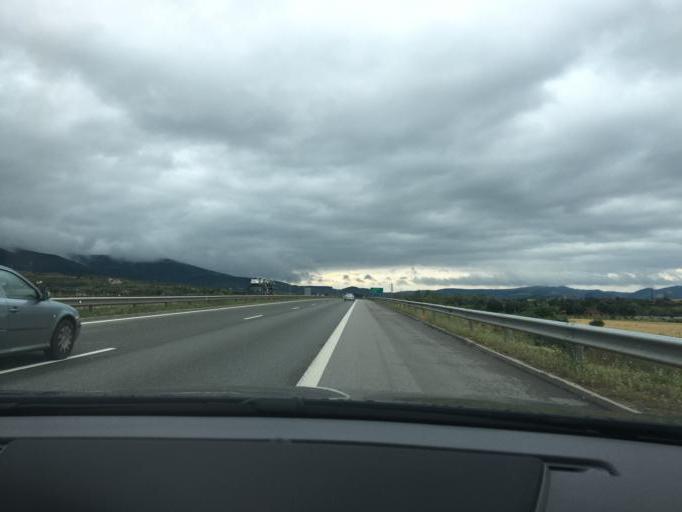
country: BG
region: Sofiya
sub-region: Obshtina Bozhurishte
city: Bozhurishte
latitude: 42.6925
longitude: 23.1750
